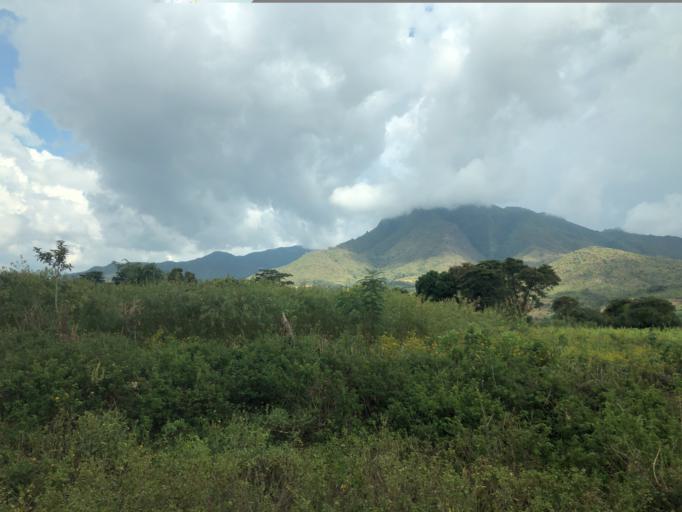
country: ET
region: Southern Nations, Nationalities, and People's Region
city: Jinka
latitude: 5.7011
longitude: 36.6309
